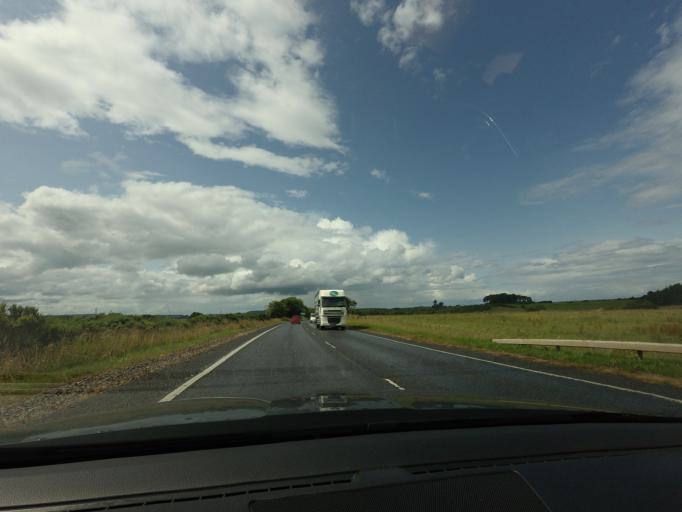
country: GB
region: Scotland
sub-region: Moray
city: Lhanbryd
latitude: 57.6342
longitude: -3.2286
